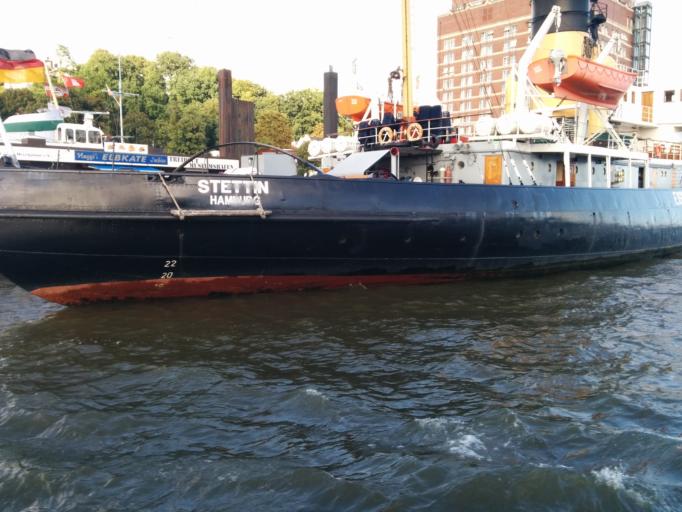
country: DE
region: Hamburg
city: Altona
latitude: 53.5434
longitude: 9.9146
